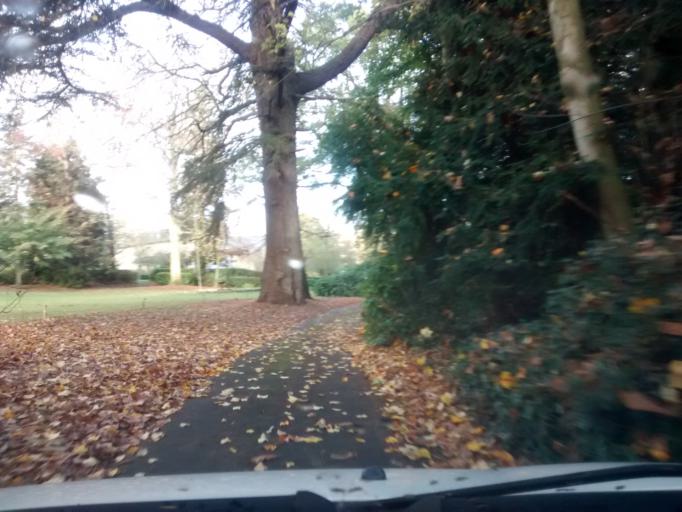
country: FR
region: Brittany
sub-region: Departement d'Ille-et-Vilaine
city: Acigne
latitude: 48.1186
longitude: -1.5564
